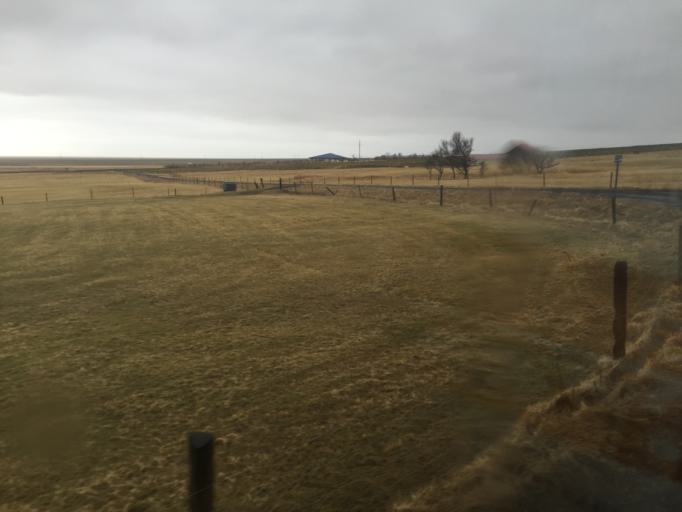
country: IS
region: East
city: Hoefn
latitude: 63.9066
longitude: -16.7068
